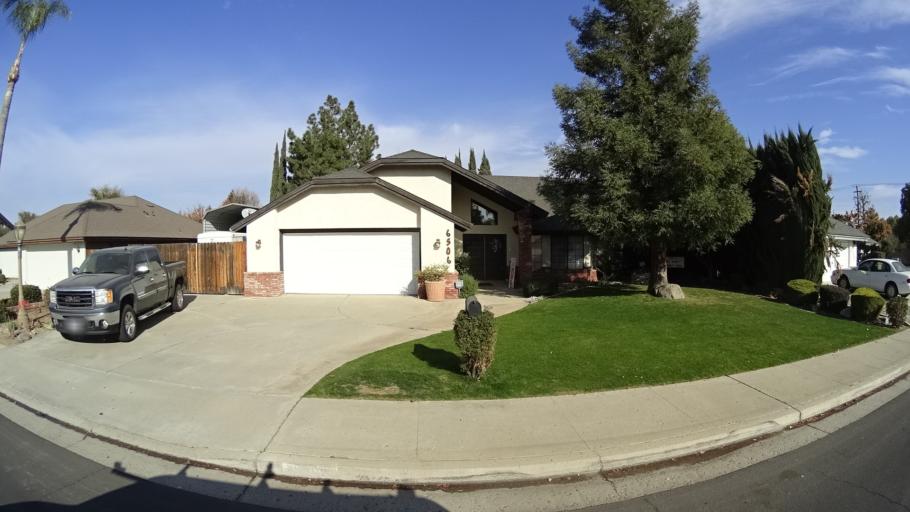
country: US
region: California
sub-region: Kern County
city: Greenacres
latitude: 35.4083
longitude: -119.0750
